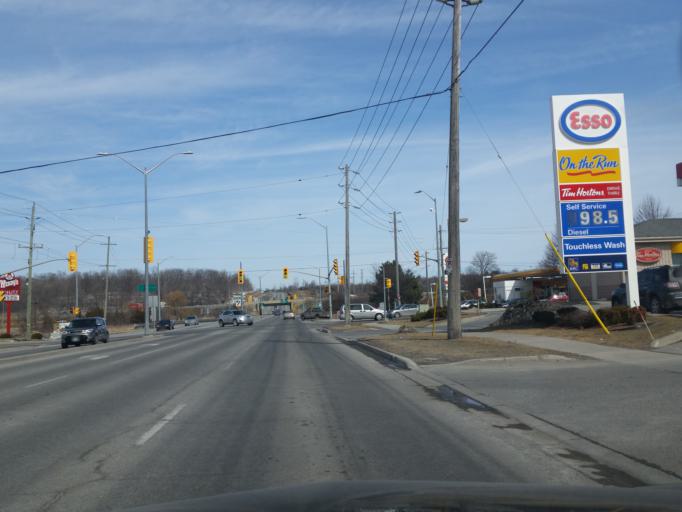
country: CA
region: Ontario
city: Kingston
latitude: 44.2656
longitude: -76.4985
